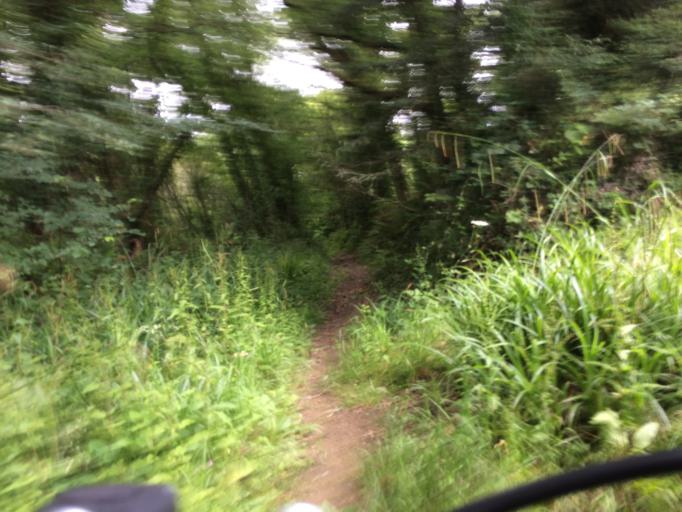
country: FR
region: Brittany
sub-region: Departement du Finistere
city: Hopital-Camfrout
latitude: 48.3295
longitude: -4.2579
